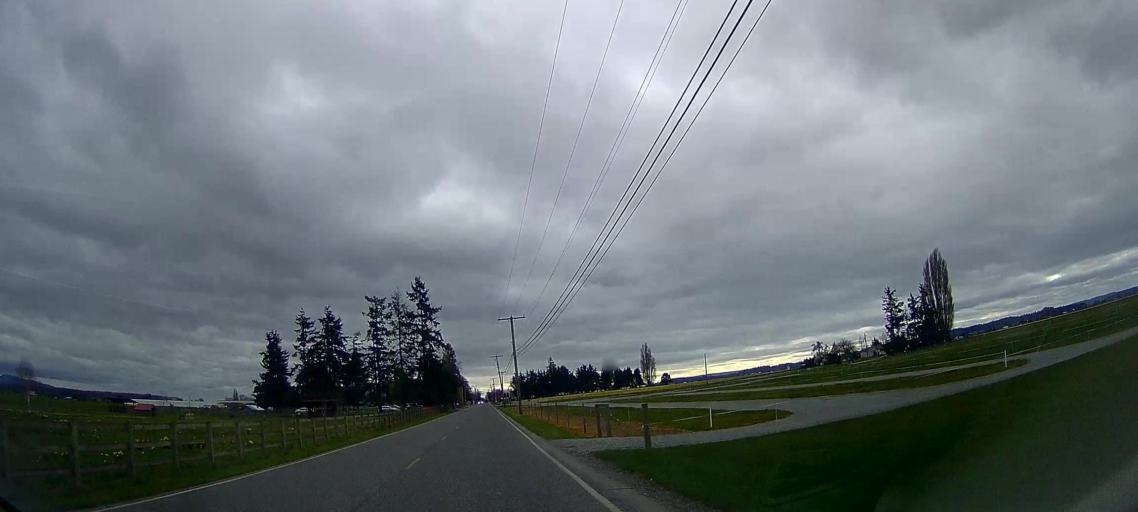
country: US
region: Washington
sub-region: Skagit County
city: Mount Vernon
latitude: 48.4184
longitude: -122.4010
